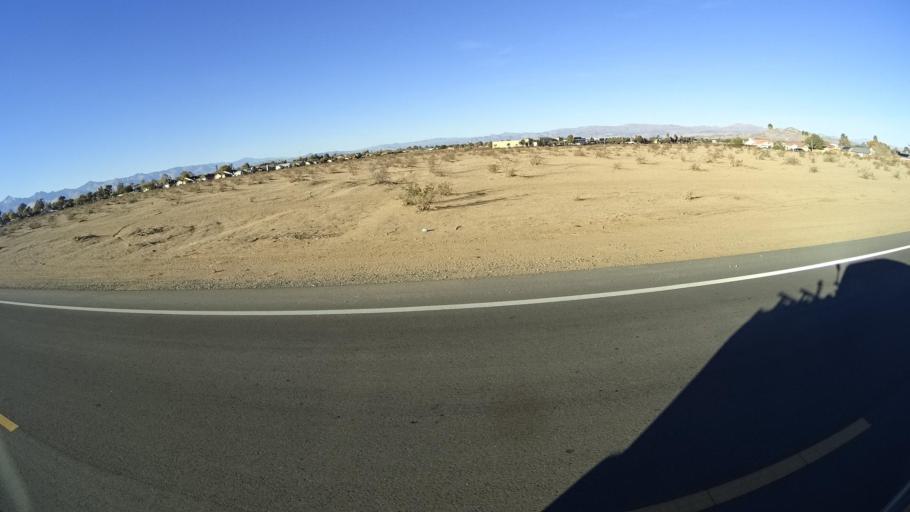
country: US
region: California
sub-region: Kern County
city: Ridgecrest
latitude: 35.6007
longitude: -117.6759
